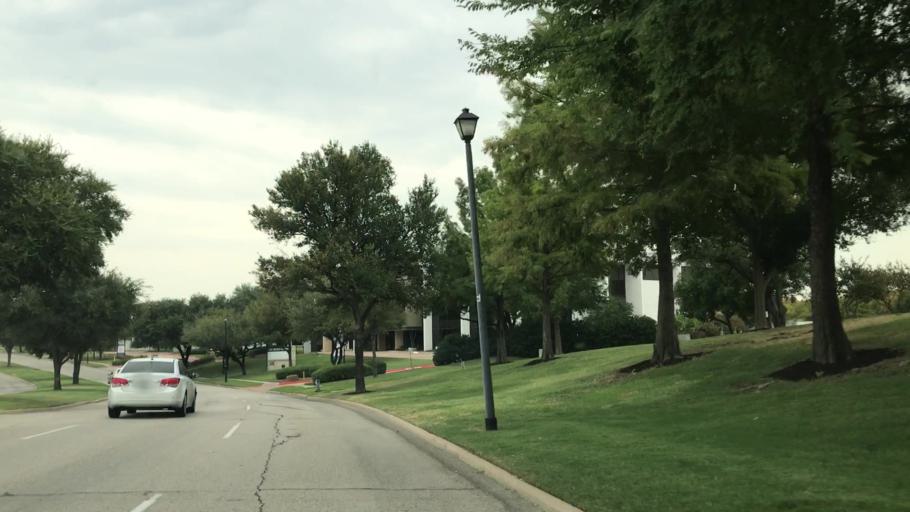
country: US
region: Texas
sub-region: Dallas County
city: Irving
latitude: 32.8815
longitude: -96.9751
